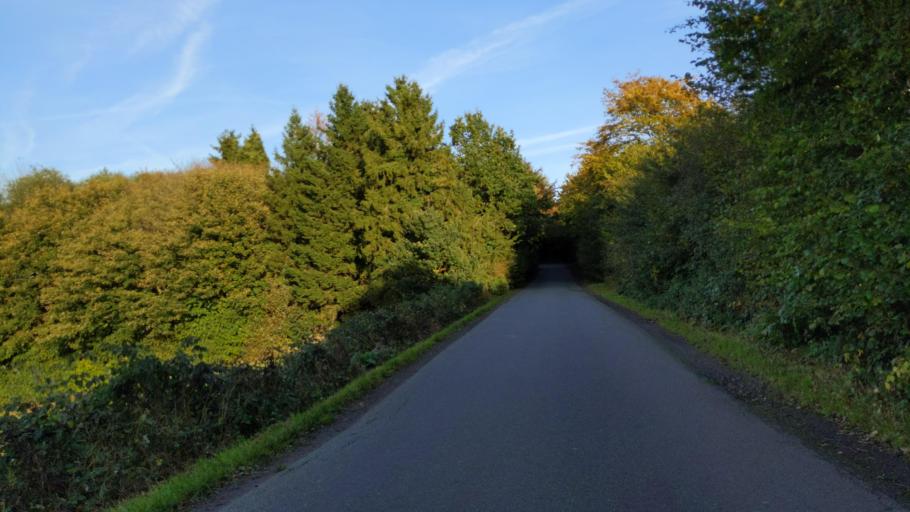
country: DE
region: Schleswig-Holstein
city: Susel
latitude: 54.0844
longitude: 10.6770
